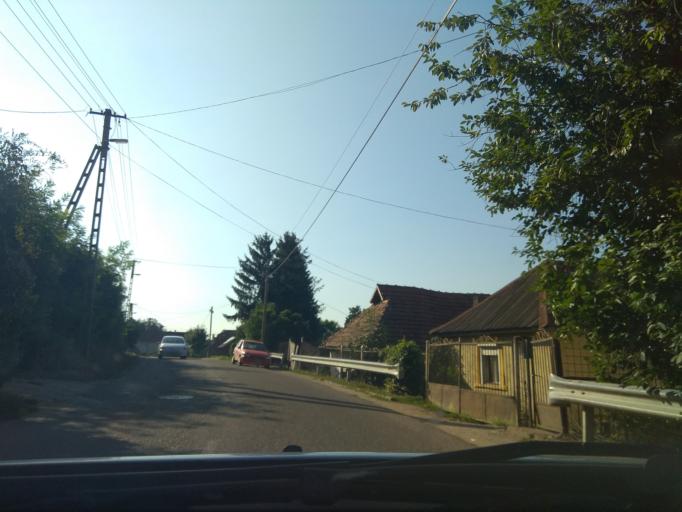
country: HU
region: Borsod-Abauj-Zemplen
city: Harsany
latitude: 47.9869
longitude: 20.7785
